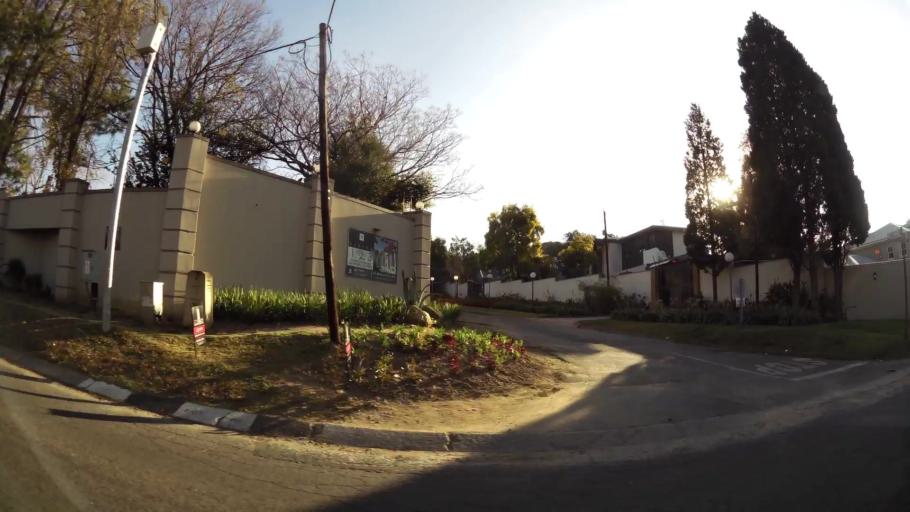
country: ZA
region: Gauteng
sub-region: City of Johannesburg Metropolitan Municipality
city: Modderfontein
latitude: -26.0872
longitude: 28.0694
